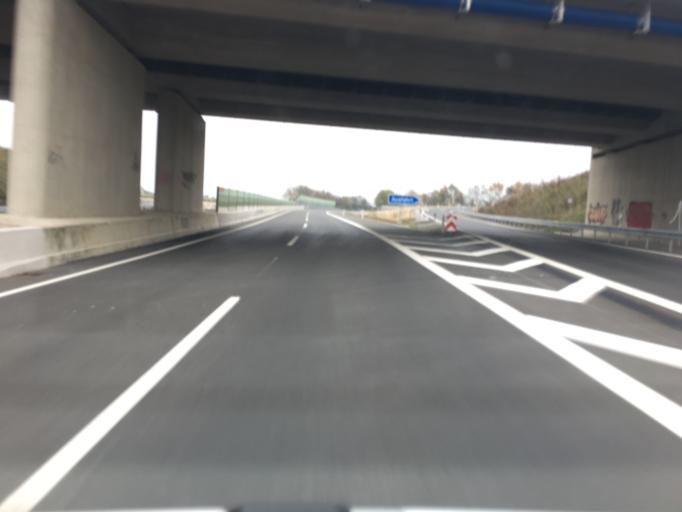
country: DE
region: North Rhine-Westphalia
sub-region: Regierungsbezirk Dusseldorf
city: Velbert
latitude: 51.3285
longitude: 7.0131
